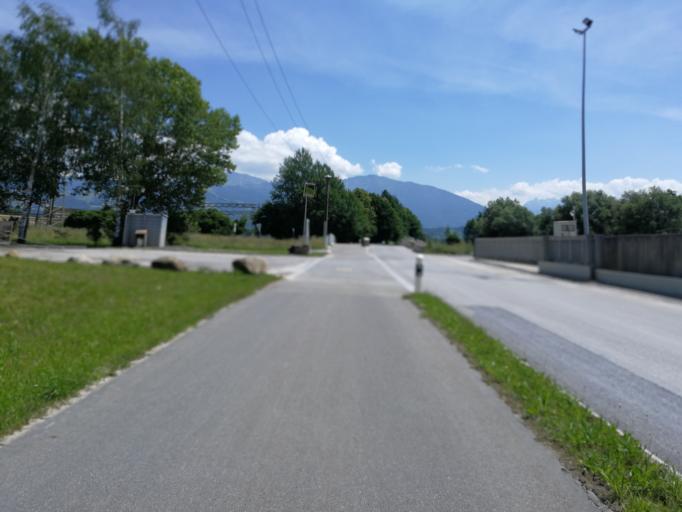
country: CH
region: Saint Gallen
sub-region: Wahlkreis See-Gaster
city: Uznach
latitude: 47.2194
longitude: 8.9692
